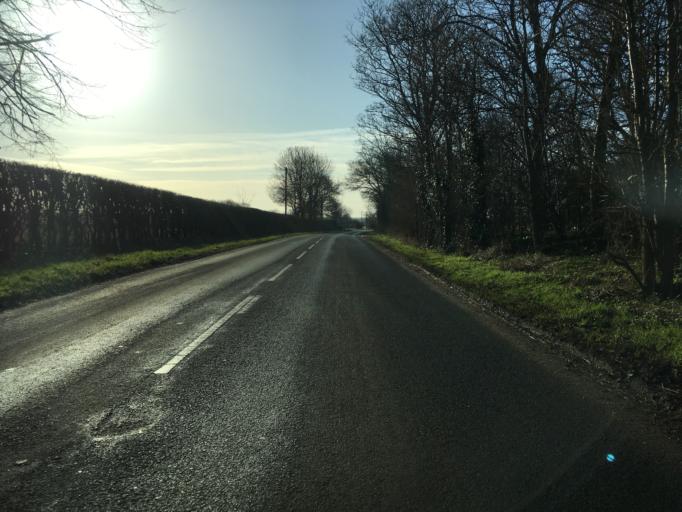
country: GB
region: England
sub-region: Warwickshire
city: Wellesbourne Mountford
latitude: 52.2014
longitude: -1.6170
